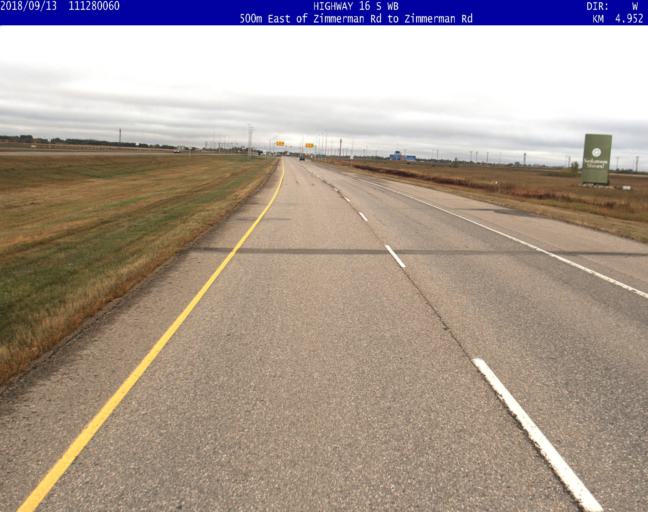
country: CA
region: Saskatchewan
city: Saskatoon
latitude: 52.0862
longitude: -106.5263
